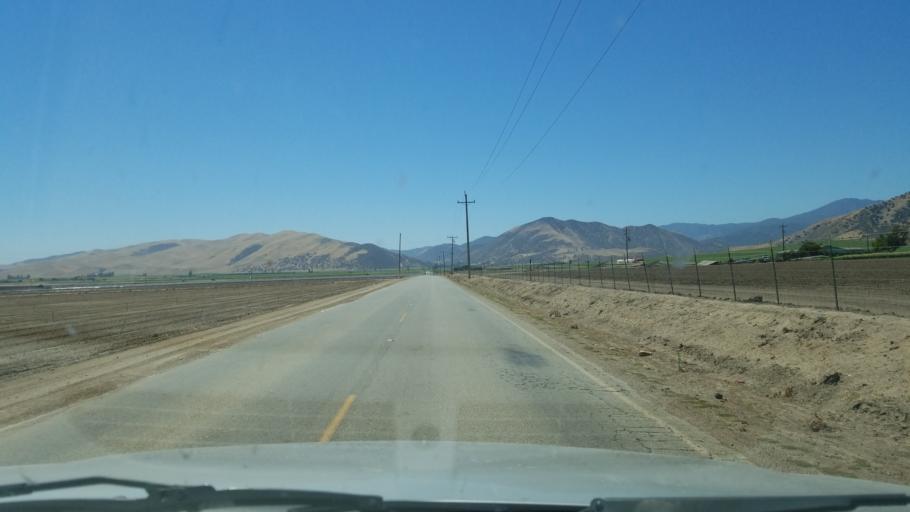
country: US
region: California
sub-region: Monterey County
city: Greenfield
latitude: 36.3301
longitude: -121.3154
